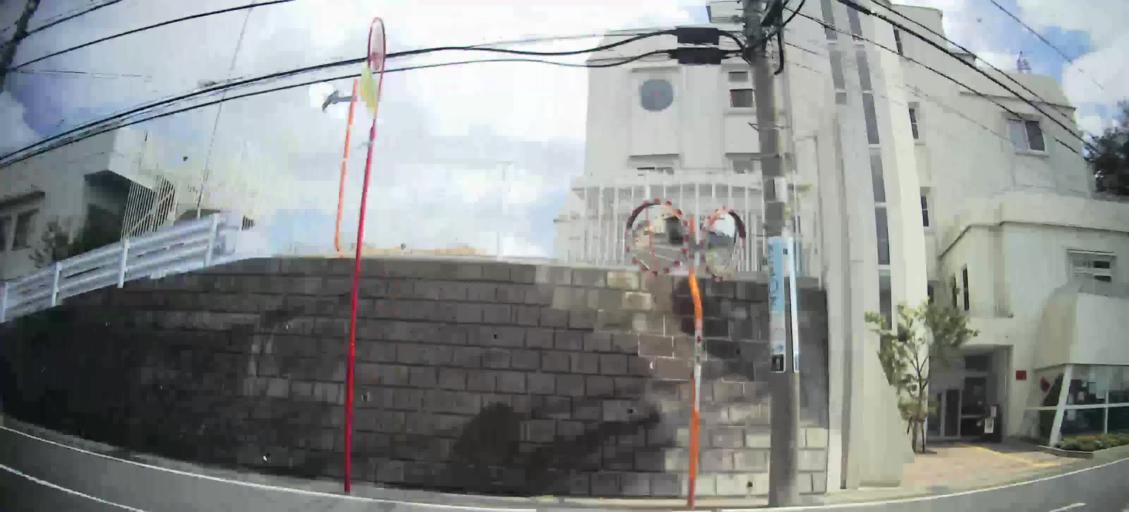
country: JP
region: Kanagawa
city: Yokohama
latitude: 35.4857
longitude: 139.5517
